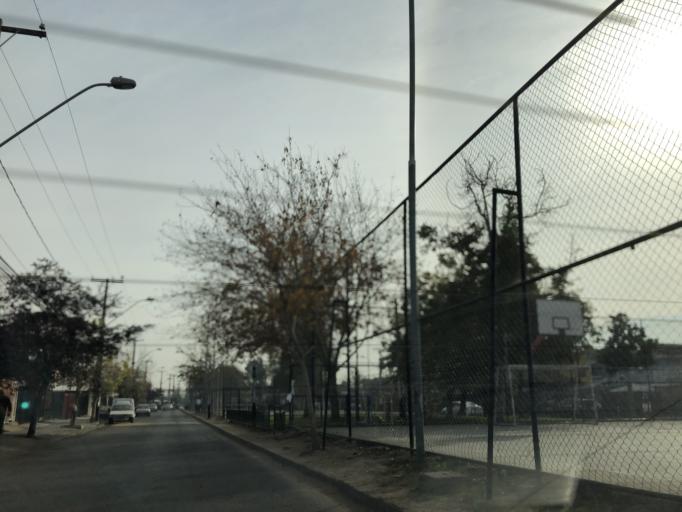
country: CL
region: Santiago Metropolitan
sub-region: Provincia de Cordillera
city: Puente Alto
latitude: -33.5831
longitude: -70.5559
